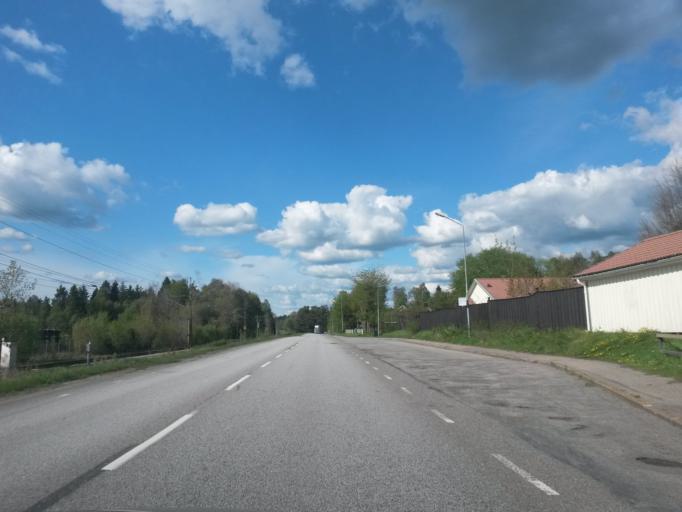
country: SE
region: Vaestra Goetaland
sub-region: Boras Kommun
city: Boras
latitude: 57.8310
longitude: 13.0108
